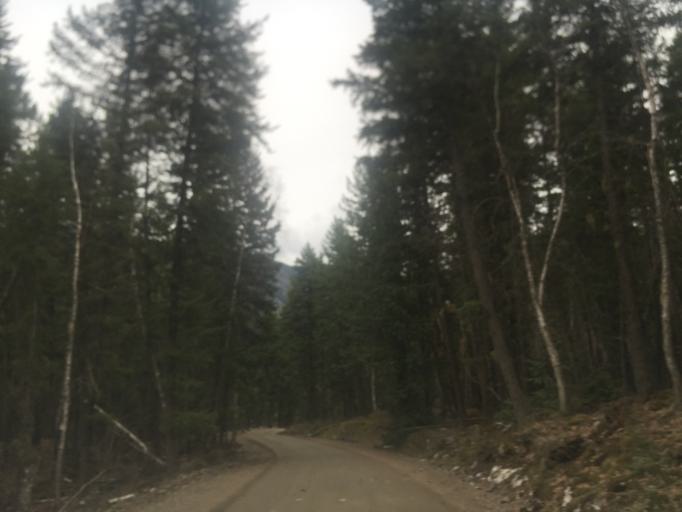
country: CA
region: British Columbia
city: Chase
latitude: 51.3749
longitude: -120.1434
